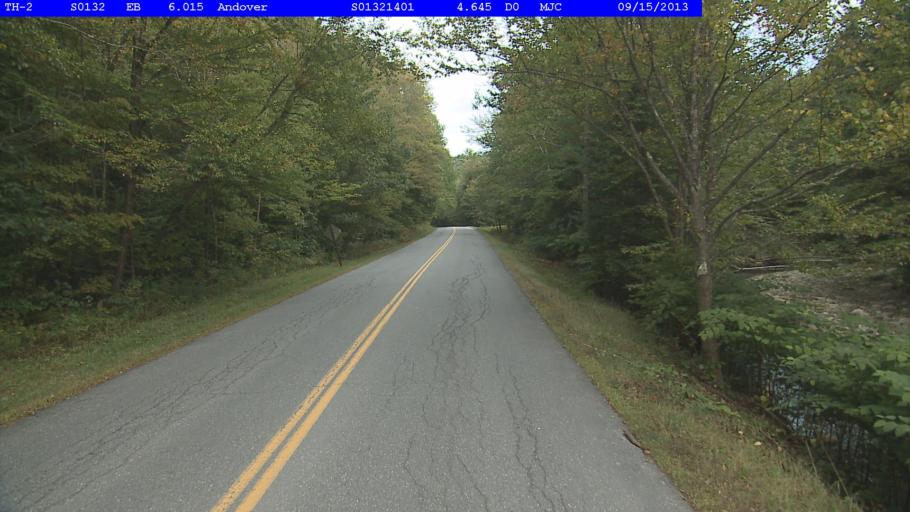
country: US
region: Vermont
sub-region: Windsor County
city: Chester
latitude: 43.2723
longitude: -72.6873
